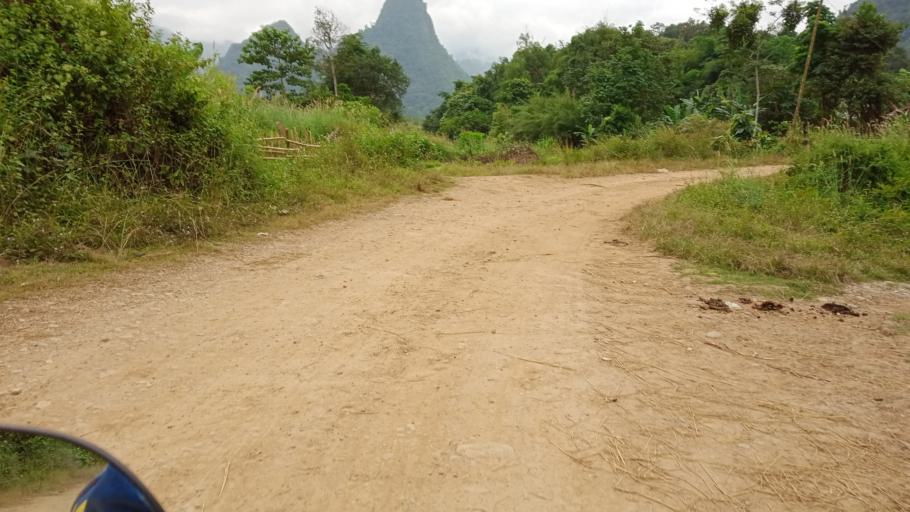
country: LA
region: Xiangkhoang
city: Phonsavan
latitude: 19.0846
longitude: 103.0116
